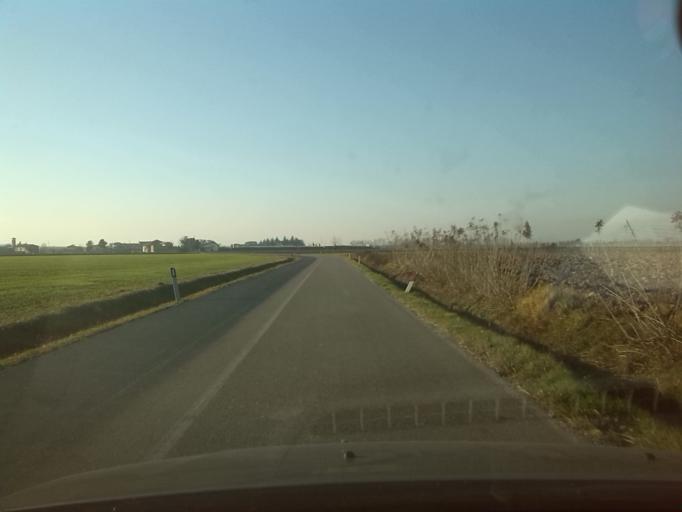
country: IT
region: Friuli Venezia Giulia
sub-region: Provincia di Udine
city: Trivignano Udinese
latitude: 45.9562
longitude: 13.3317
